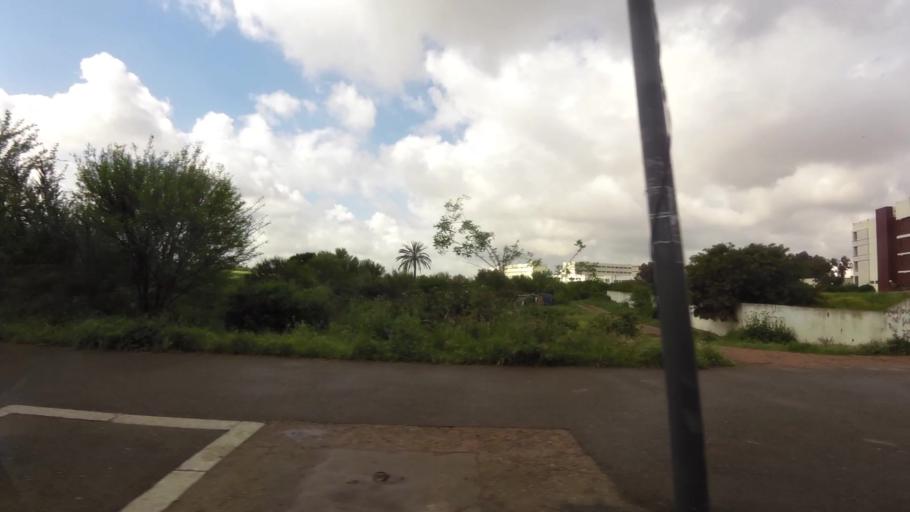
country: MA
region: Grand Casablanca
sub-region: Casablanca
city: Casablanca
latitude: 33.5425
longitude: -7.6523
